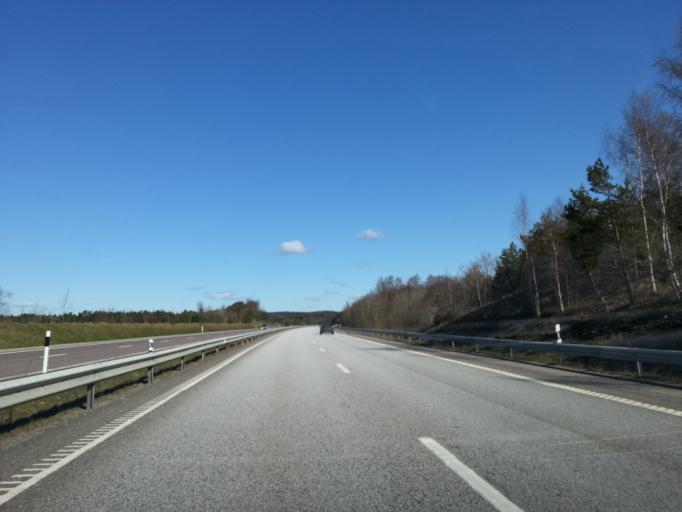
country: SE
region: Vaestra Goetaland
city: Svanesund
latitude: 58.0913
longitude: 11.8824
